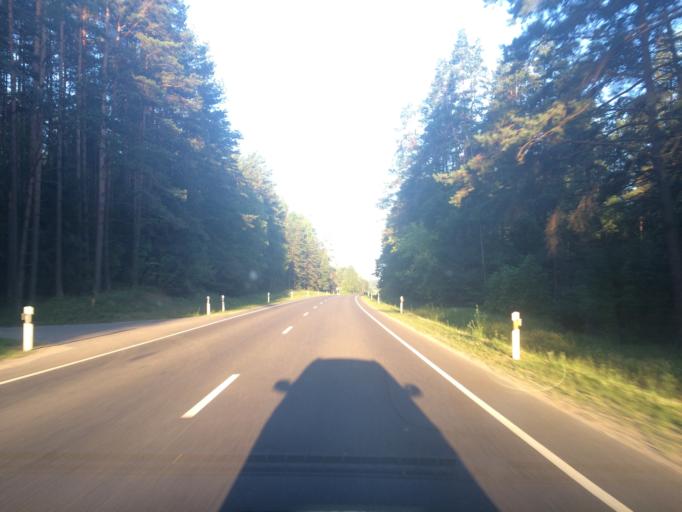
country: LT
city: Zarasai
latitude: 55.7054
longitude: 26.1772
